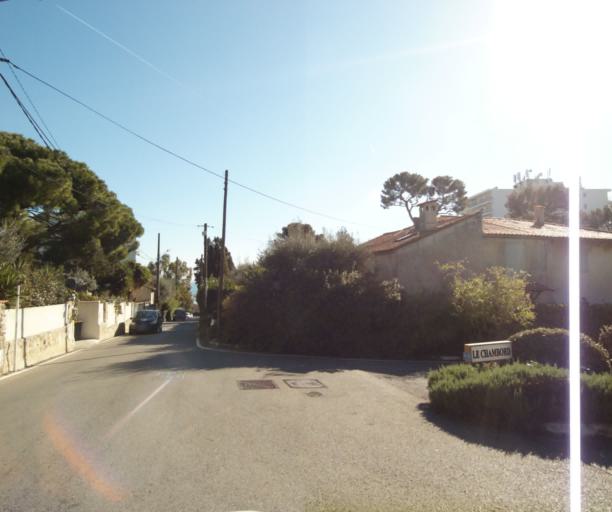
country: FR
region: Provence-Alpes-Cote d'Azur
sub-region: Departement des Alpes-Maritimes
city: Antibes
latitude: 43.5889
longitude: 7.1128
